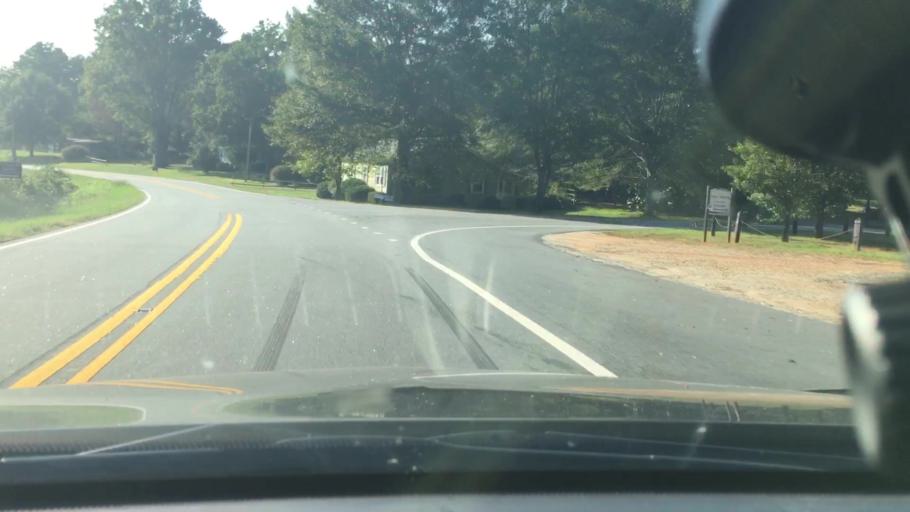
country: US
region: North Carolina
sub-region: Polk County
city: Columbus
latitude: 35.3252
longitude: -82.1051
